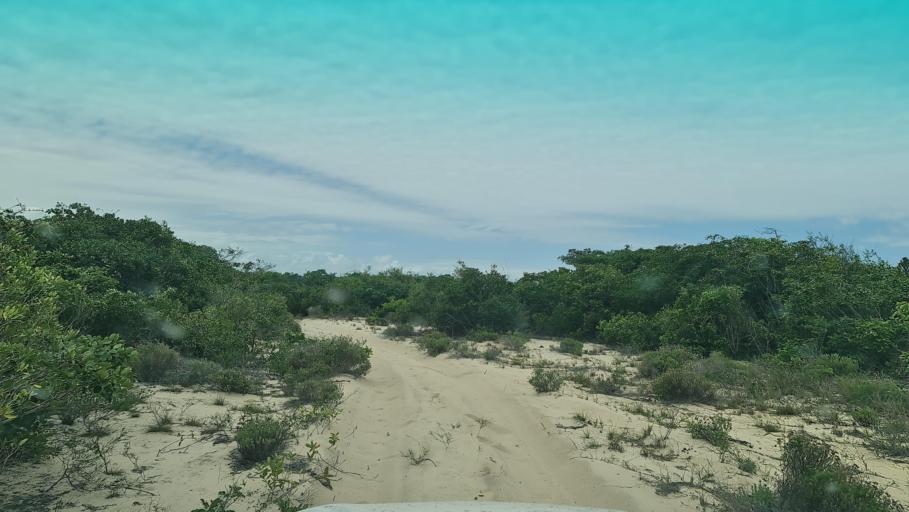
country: MZ
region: Maputo
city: Manhica
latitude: -25.6348
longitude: 32.7857
